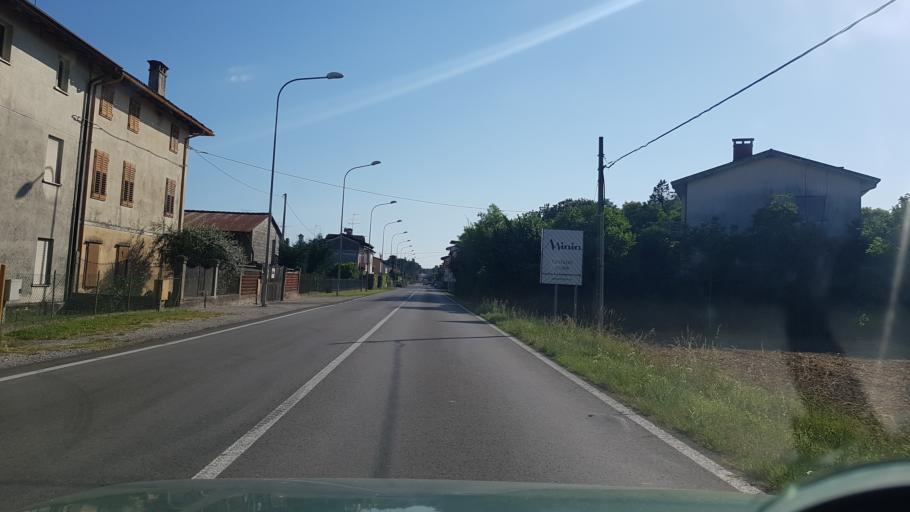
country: IT
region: Friuli Venezia Giulia
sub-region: Provincia di Udine
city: Cervignano del Friuli
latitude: 45.8287
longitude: 13.3456
